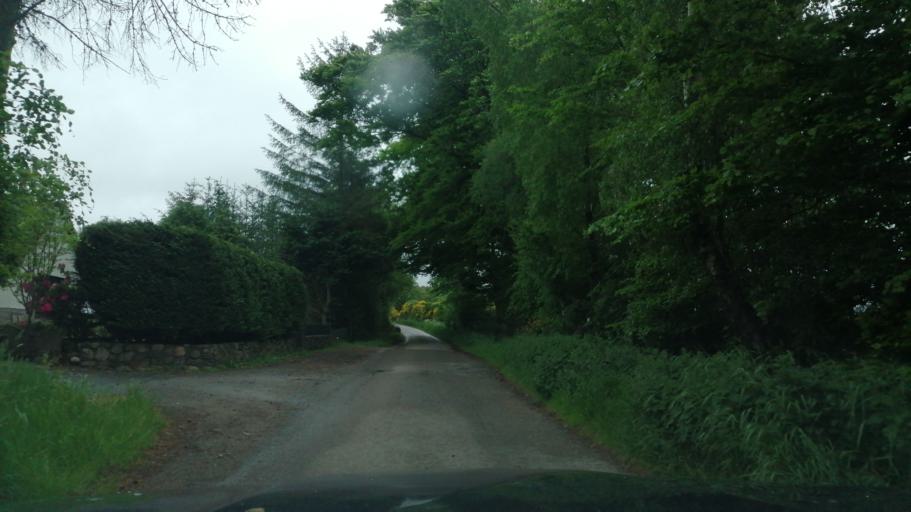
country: GB
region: Scotland
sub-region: Moray
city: Keith
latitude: 57.5653
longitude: -2.8612
